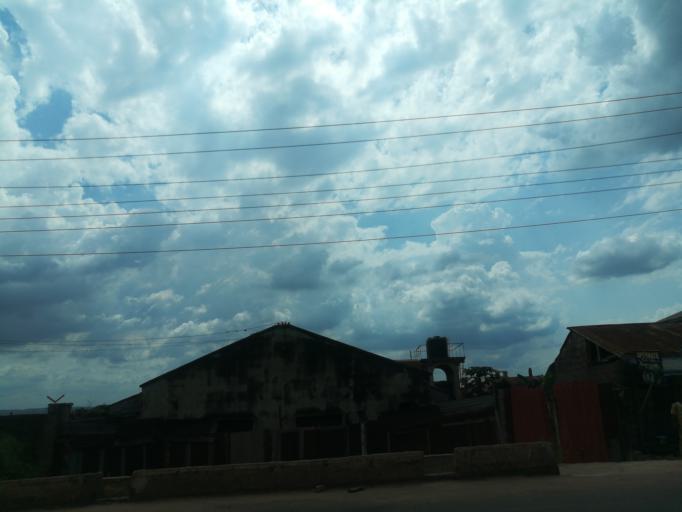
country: NG
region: Oyo
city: Ibadan
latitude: 7.4247
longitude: 3.8422
